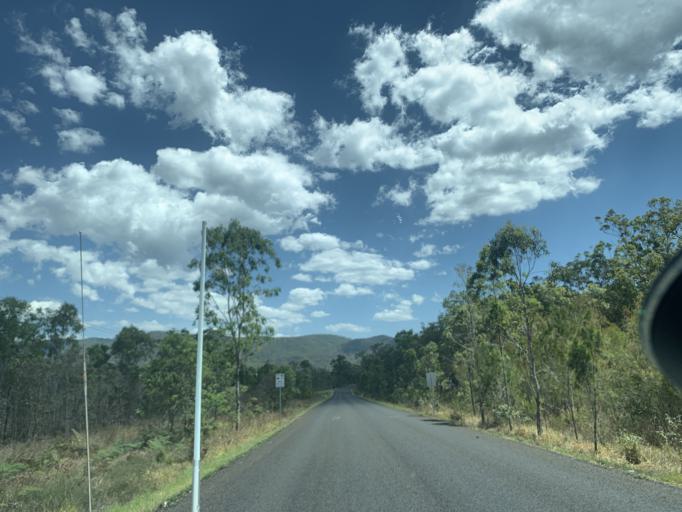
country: AU
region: Queensland
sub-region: Tablelands
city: Atherton
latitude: -17.3075
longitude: 145.4573
